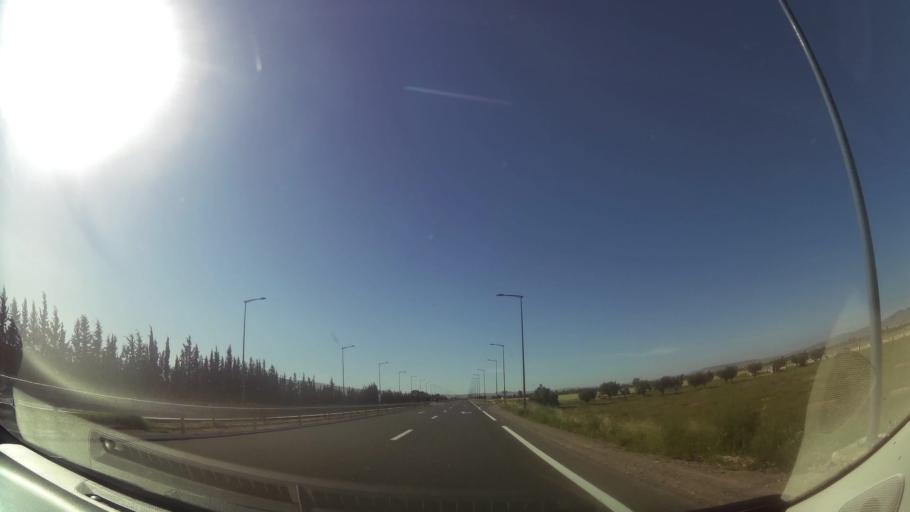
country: MA
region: Oriental
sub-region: Oujda-Angad
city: Oujda
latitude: 34.8151
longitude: -1.9640
